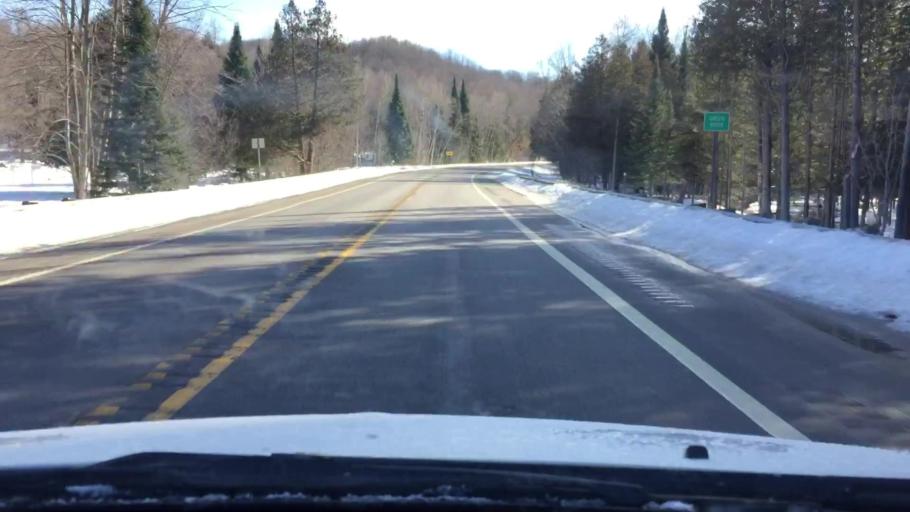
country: US
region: Michigan
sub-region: Antrim County
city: Mancelona
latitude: 45.0068
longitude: -85.0638
